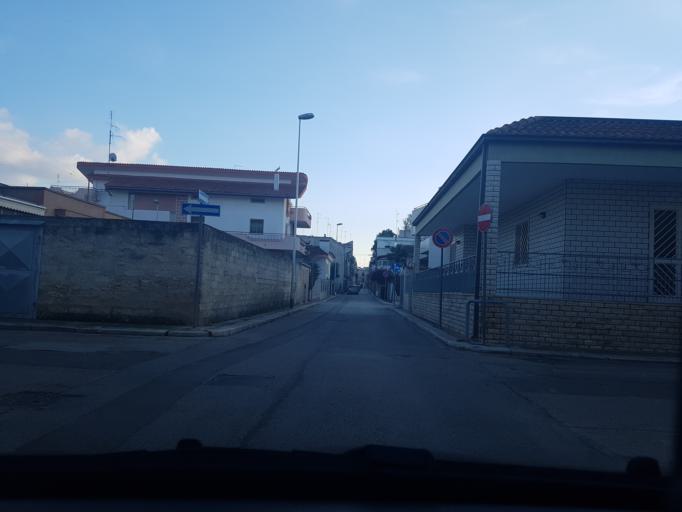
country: IT
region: Apulia
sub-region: Provincia di Bari
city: Bitritto
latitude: 41.0444
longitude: 16.8253
